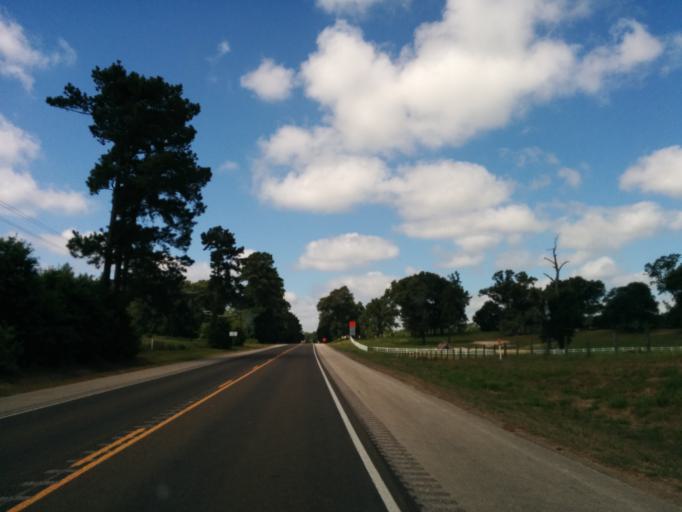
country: US
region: Texas
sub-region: Houston County
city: Hickory Creek
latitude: 31.3660
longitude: -95.1745
